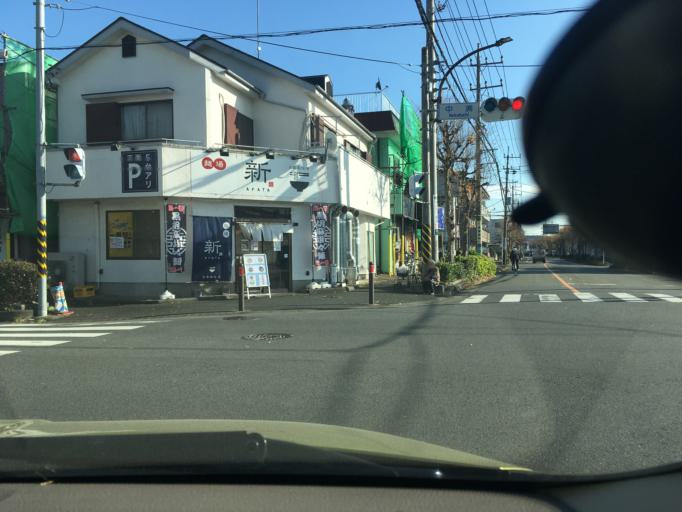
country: JP
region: Tokyo
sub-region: Machida-shi
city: Machida
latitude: 35.5641
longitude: 139.4090
